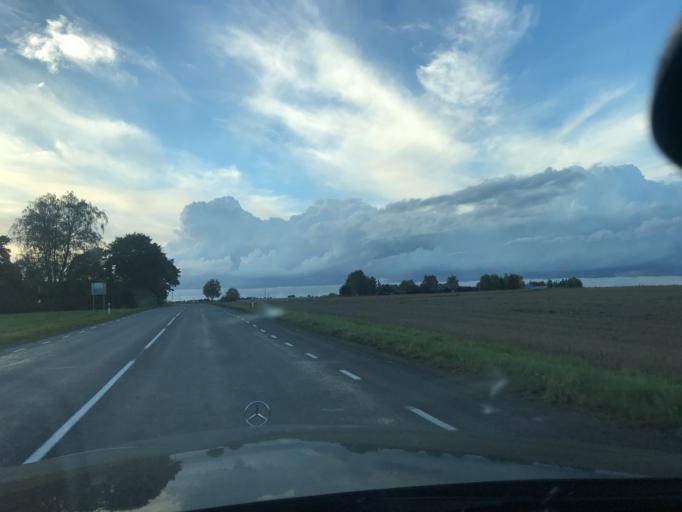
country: EE
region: Vorumaa
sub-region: Antsla vald
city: Vana-Antsla
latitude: 57.8857
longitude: 26.5235
